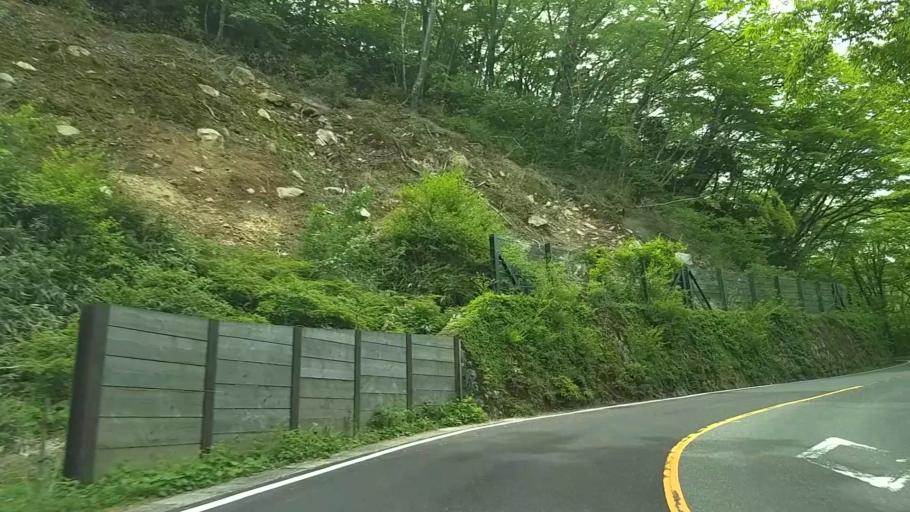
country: JP
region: Kanagawa
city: Hakone
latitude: 35.2490
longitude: 139.0205
